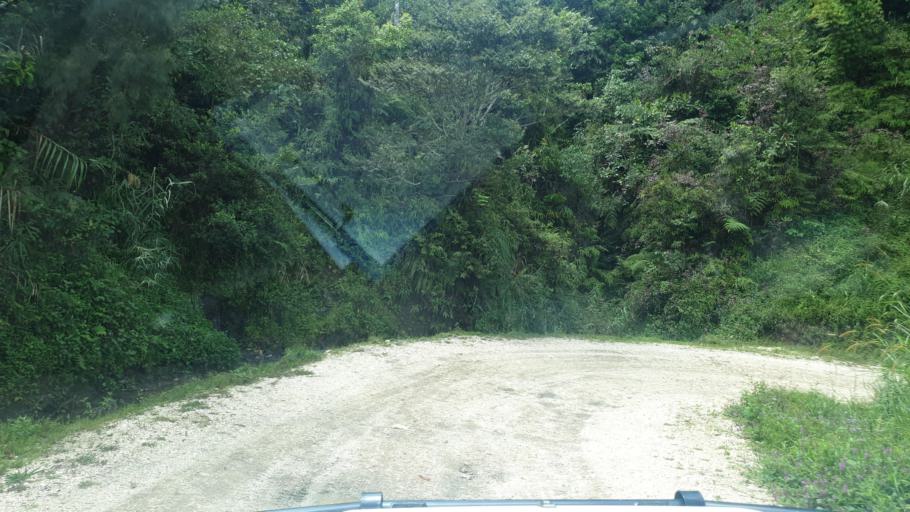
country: PG
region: Chimbu
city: Kundiawa
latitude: -6.2115
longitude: 145.1382
